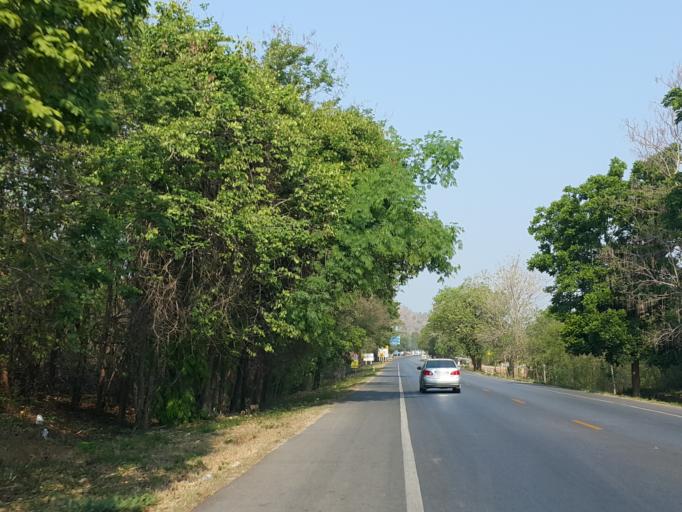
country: TH
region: Kanchanaburi
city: Sai Yok
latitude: 14.0898
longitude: 99.2871
